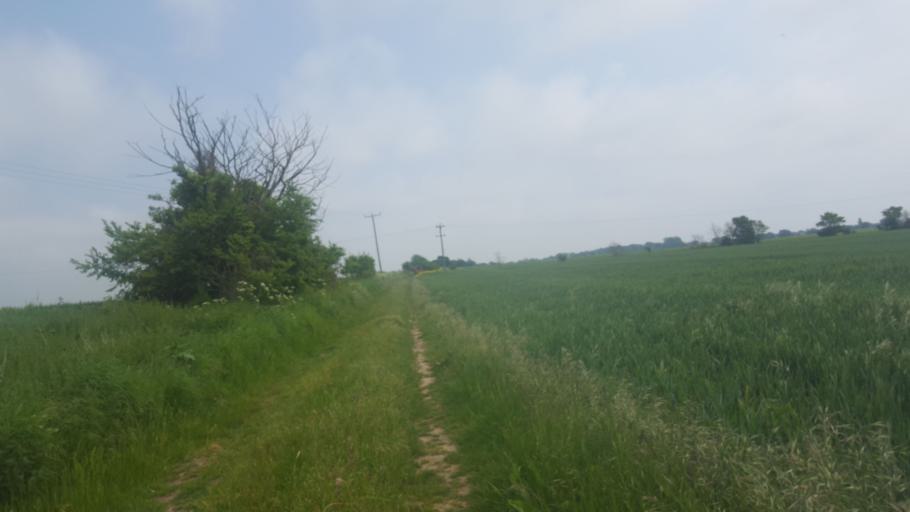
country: GB
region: England
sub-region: Essex
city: Saint Osyth
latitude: 51.7932
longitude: 1.0961
